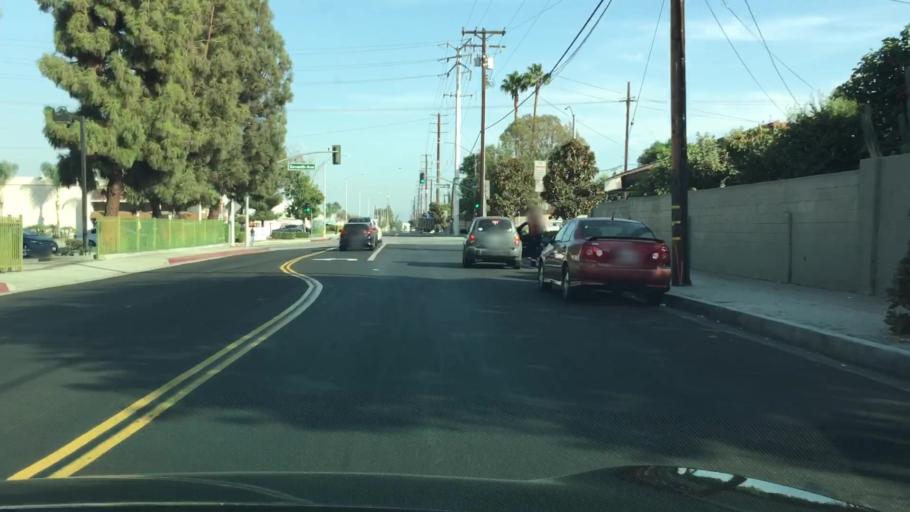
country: US
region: California
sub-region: Los Angeles County
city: Avocado Heights
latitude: 34.0236
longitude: -117.9867
